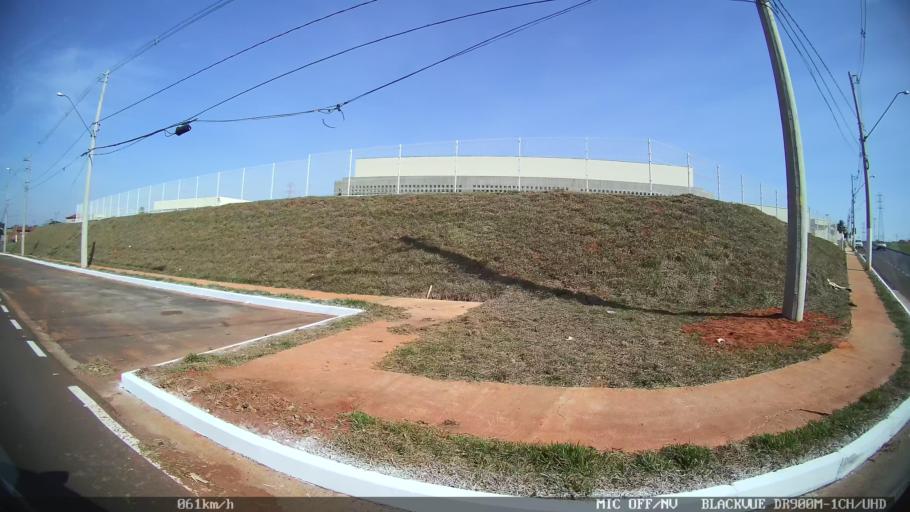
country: BR
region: Sao Paulo
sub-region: Sao Jose Do Rio Preto
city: Sao Jose do Rio Preto
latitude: -20.7891
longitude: -49.4141
